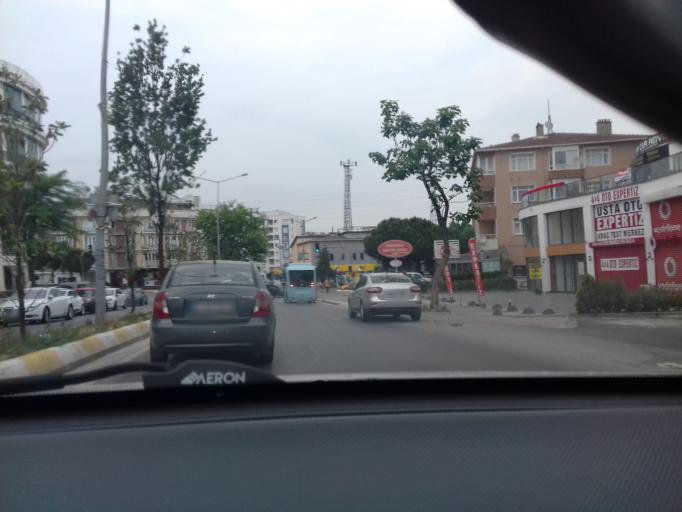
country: TR
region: Istanbul
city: Pendik
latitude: 40.9126
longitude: 29.2985
